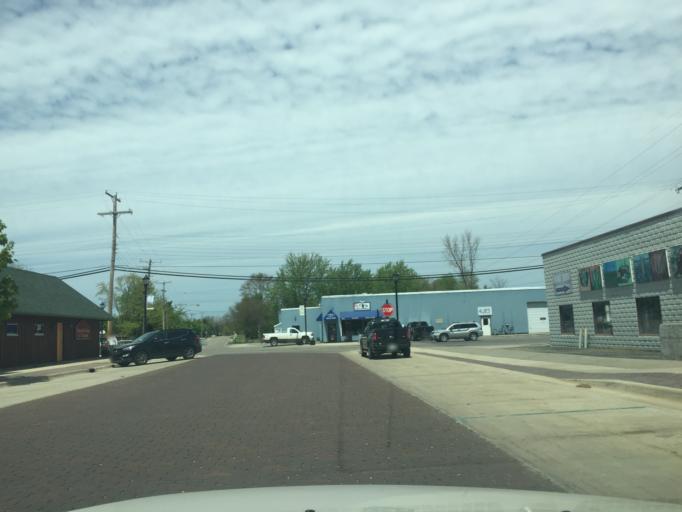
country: US
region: Michigan
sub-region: Berrien County
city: Stevensville
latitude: 41.9569
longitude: -86.4857
